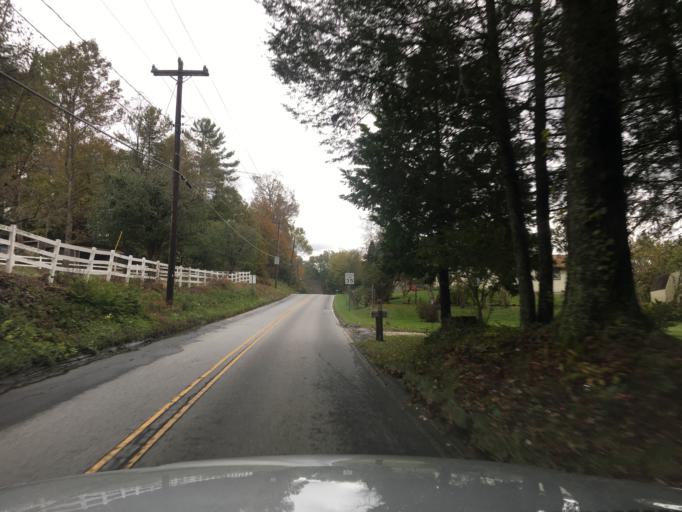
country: US
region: North Carolina
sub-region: Henderson County
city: Valley Hill
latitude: 35.2979
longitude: -82.4878
